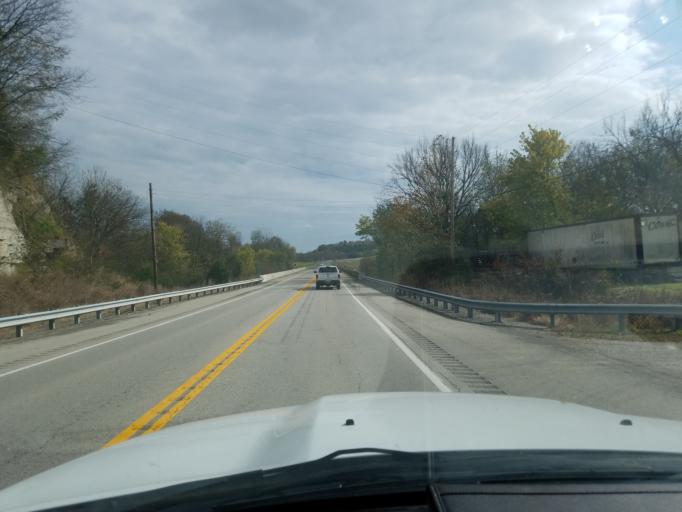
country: US
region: Kentucky
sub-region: Bullitt County
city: Mount Washington
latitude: 38.0132
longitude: -85.5137
